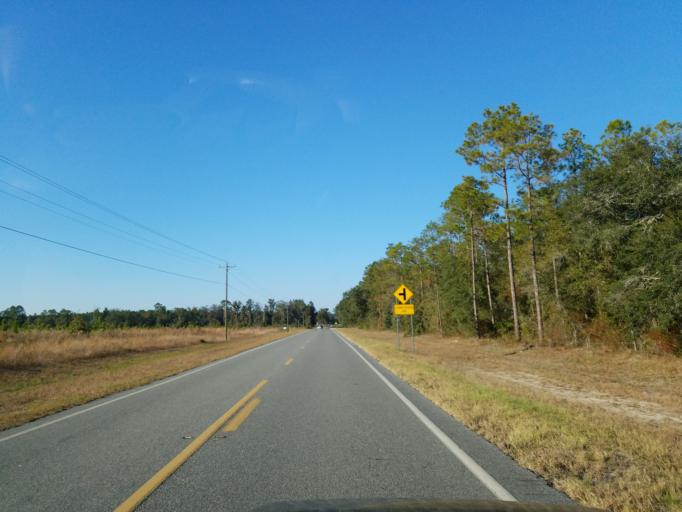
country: US
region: Georgia
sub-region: Echols County
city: Statenville
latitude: 30.6907
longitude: -83.0623
